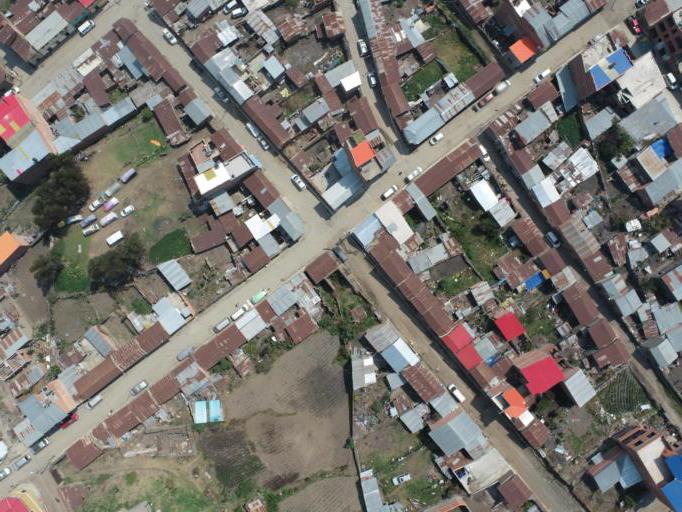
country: BO
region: La Paz
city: Quime
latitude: -16.9828
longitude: -67.2161
